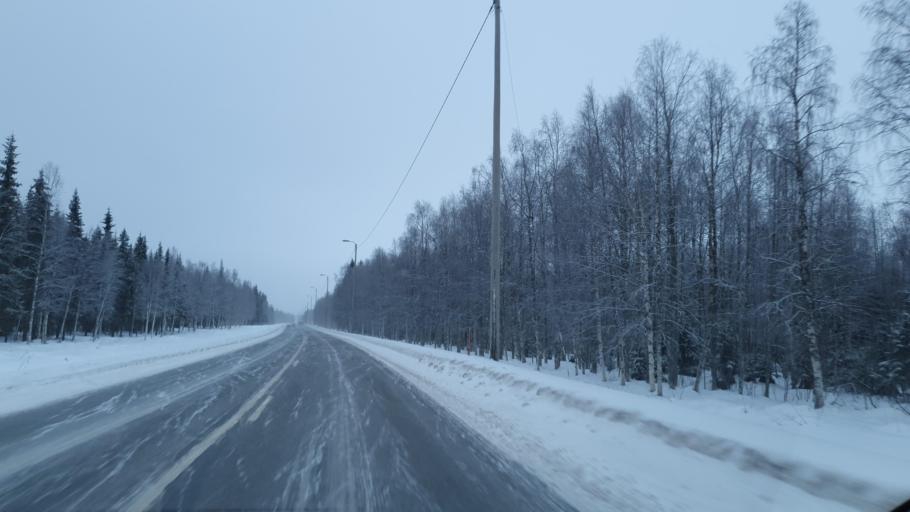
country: FI
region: Lapland
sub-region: Torniolaakso
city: Ylitornio
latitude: 66.2510
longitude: 23.7168
